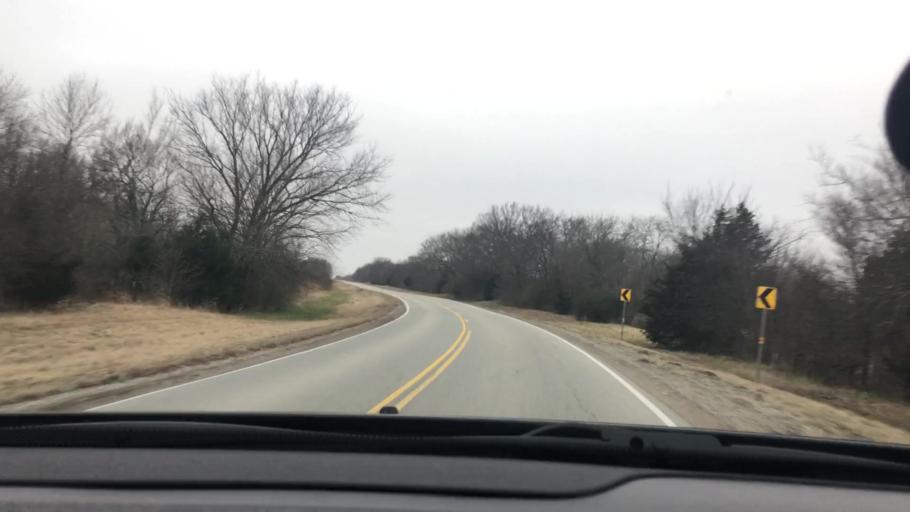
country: US
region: Oklahoma
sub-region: Coal County
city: Coalgate
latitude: 34.5306
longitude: -96.2618
